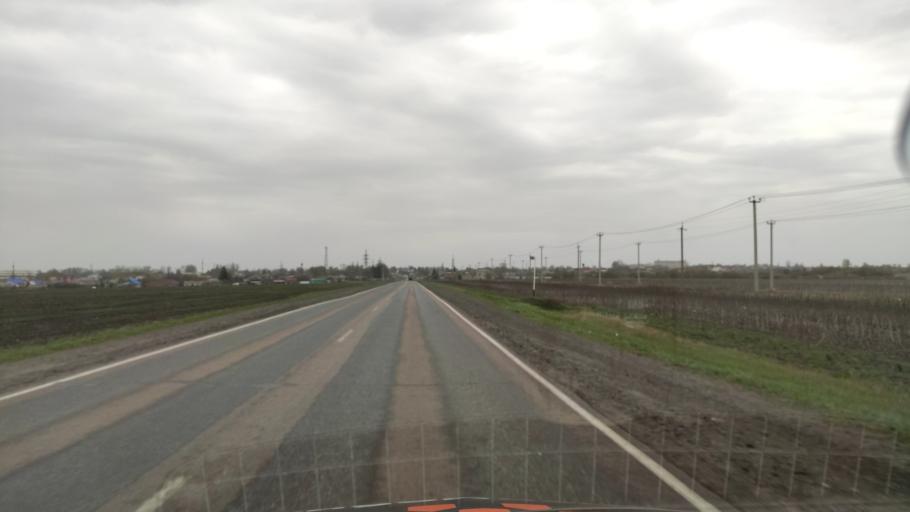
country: RU
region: Kursk
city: Gorshechnoye
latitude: 51.5111
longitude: 38.0029
